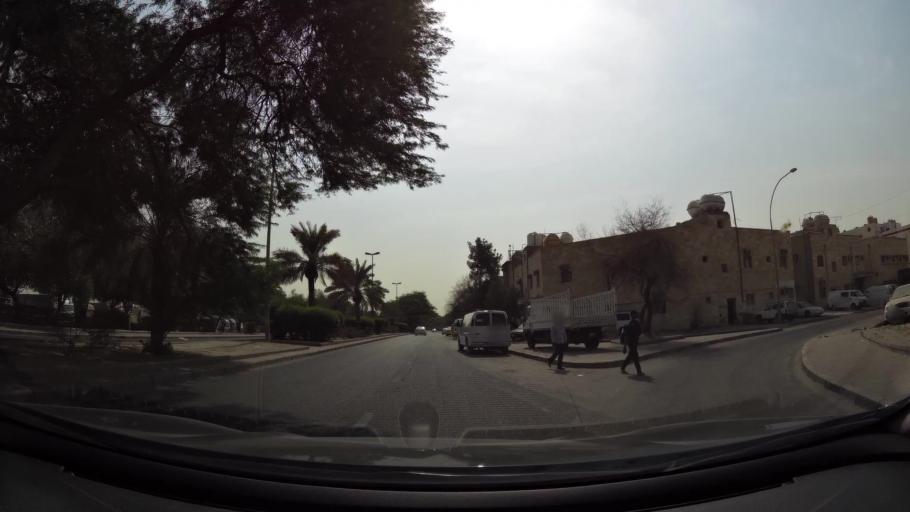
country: KW
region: Al Farwaniyah
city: Al Farwaniyah
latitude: 29.2555
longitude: 47.9456
